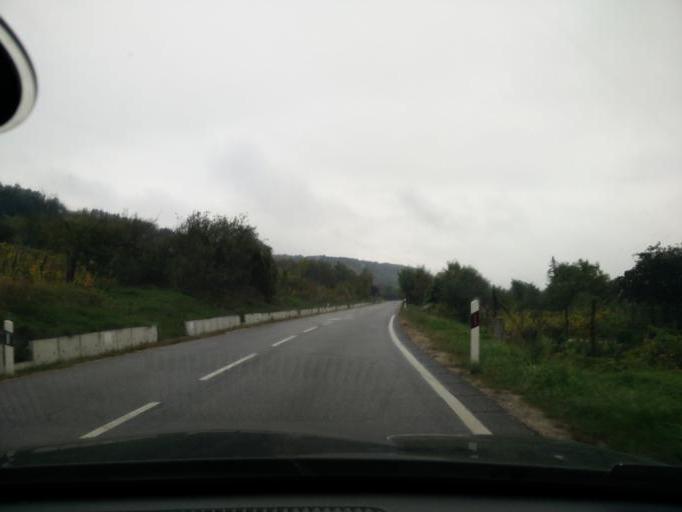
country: HU
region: Komarom-Esztergom
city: Tarjan
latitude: 47.6446
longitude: 18.5340
